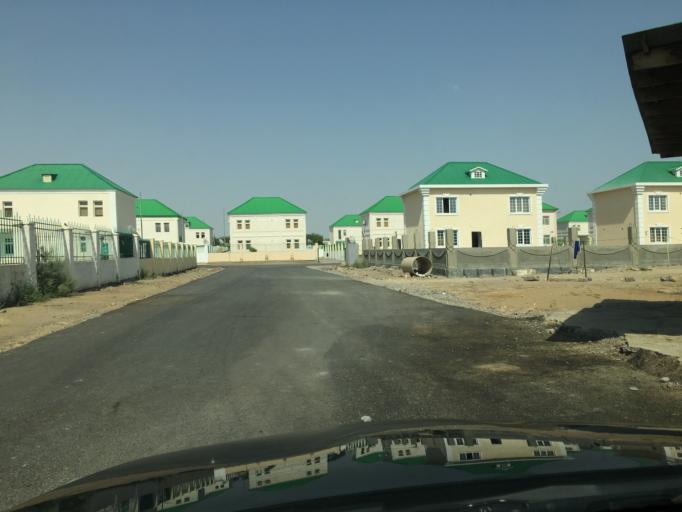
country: TM
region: Ahal
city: Ashgabat
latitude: 37.9987
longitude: 58.3989
